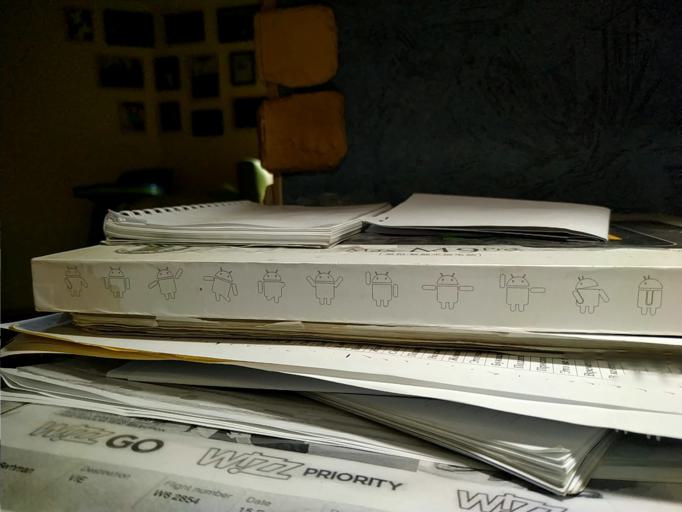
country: RU
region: Novgorod
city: Poddor'ye
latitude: 57.5274
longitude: 30.9079
